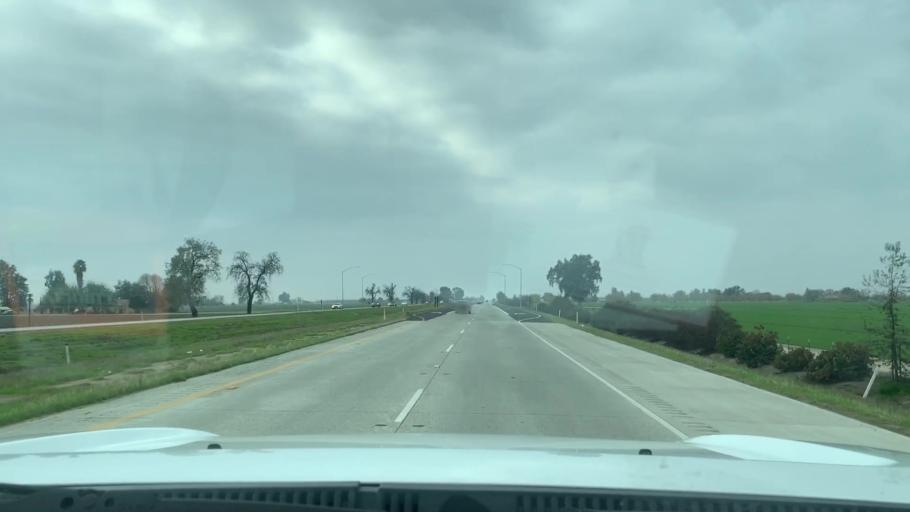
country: US
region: California
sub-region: Tulare County
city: Goshen
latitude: 36.3279
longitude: -119.4637
